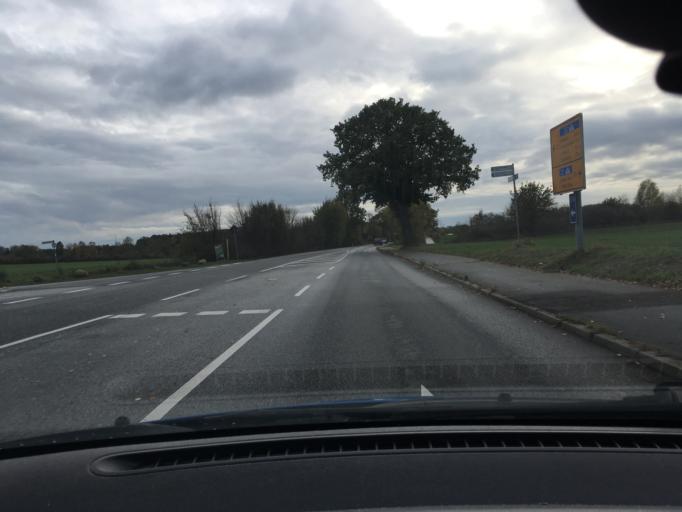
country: DE
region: Schleswig-Holstein
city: Talkau
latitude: 53.5755
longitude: 10.5683
